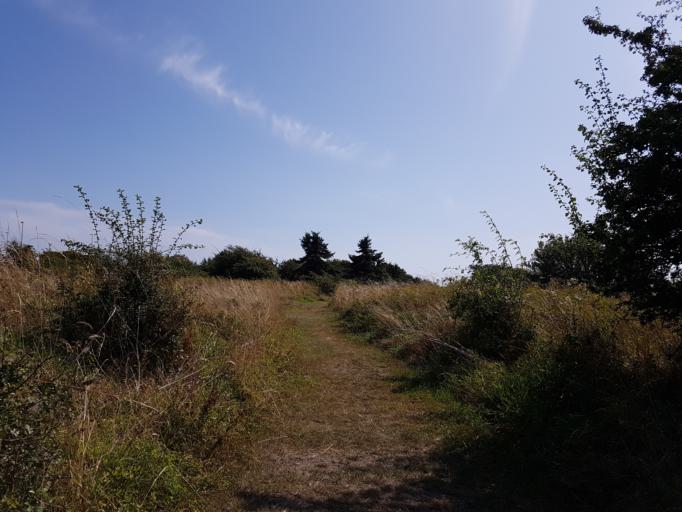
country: DK
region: Zealand
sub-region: Guldborgsund Kommune
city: Nykobing Falster
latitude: 54.5786
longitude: 11.9222
